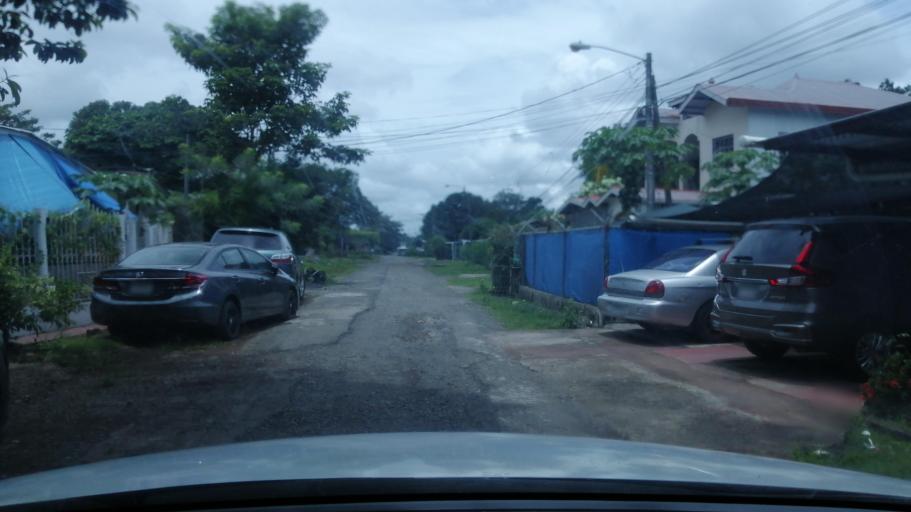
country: PA
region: Chiriqui
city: David
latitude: 8.4185
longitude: -82.4424
